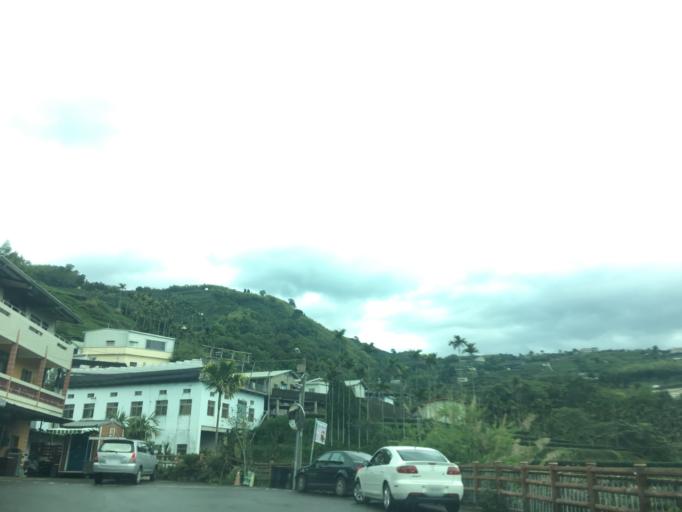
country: TW
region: Taiwan
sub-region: Yunlin
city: Douliu
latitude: 23.5577
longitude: 120.6649
